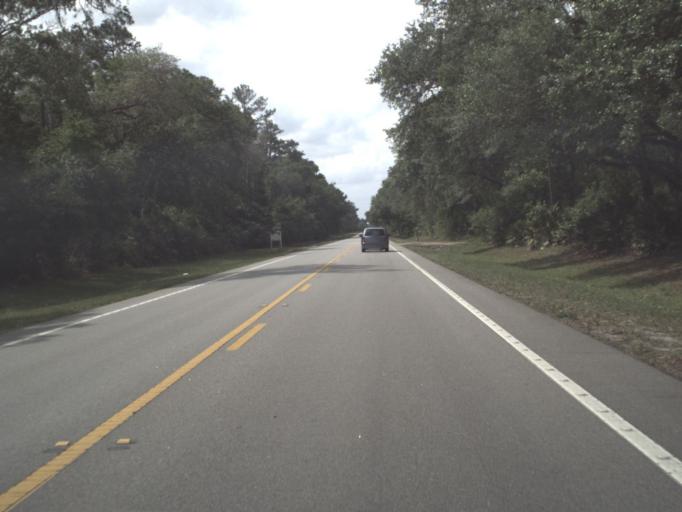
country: US
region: Florida
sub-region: Putnam County
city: Crescent City
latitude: 29.4966
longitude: -81.4813
